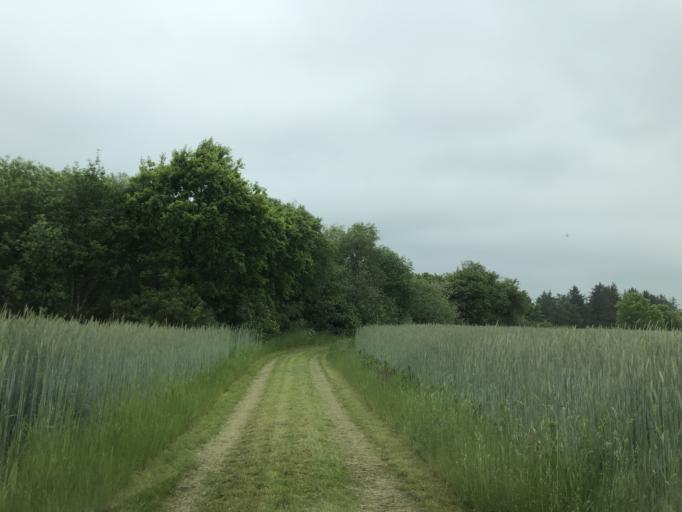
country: DK
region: Central Jutland
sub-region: Holstebro Kommune
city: Holstebro
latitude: 56.3322
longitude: 8.4811
